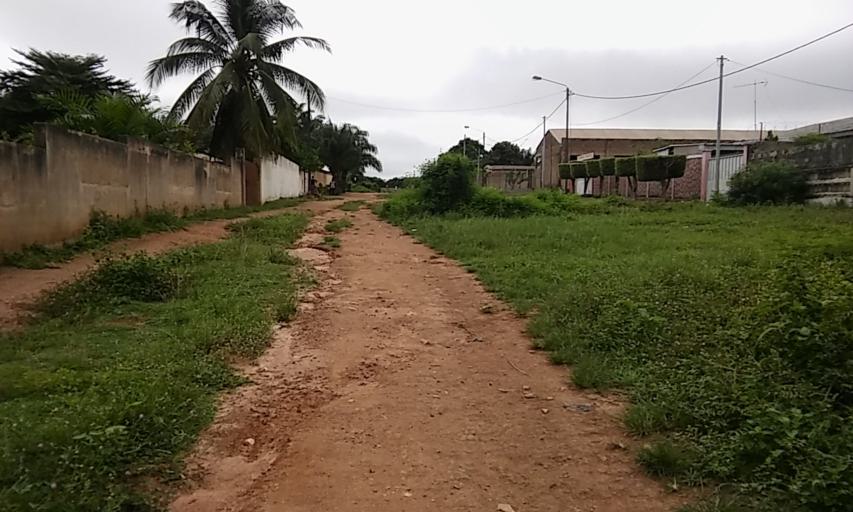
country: CI
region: Vallee du Bandama
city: Bouake
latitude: 7.6938
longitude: -5.0613
